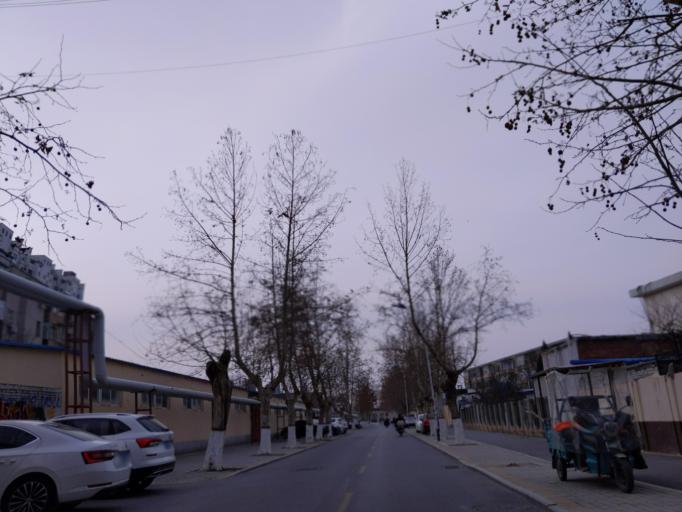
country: CN
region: Henan Sheng
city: Zhongyuanlu
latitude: 35.7597
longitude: 115.0439
